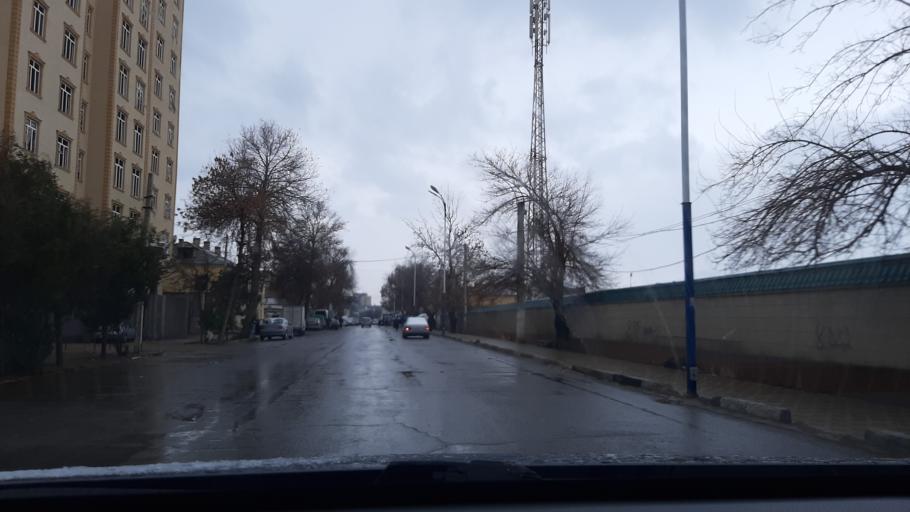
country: TJ
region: Viloyati Sughd
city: Khujand
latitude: 40.2774
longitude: 69.6388
